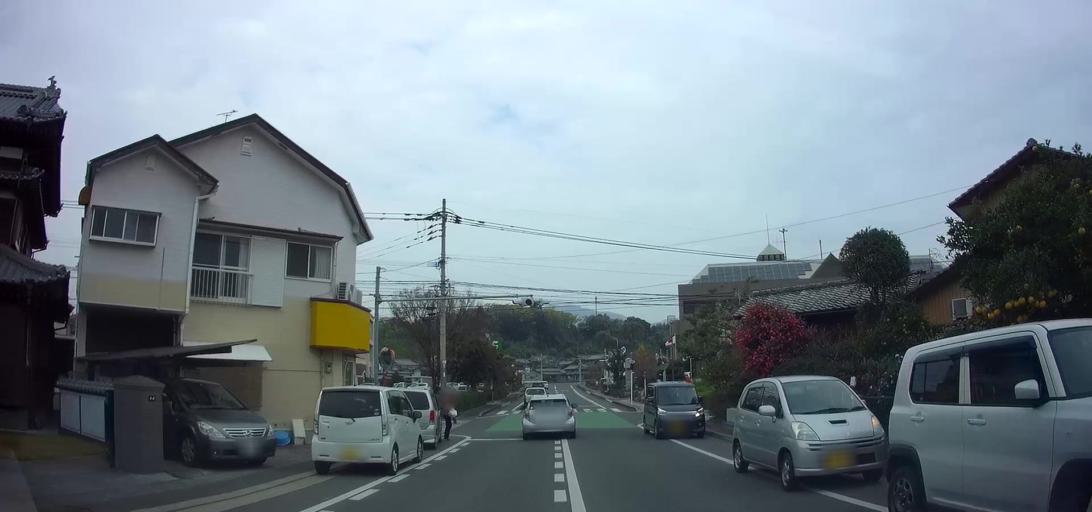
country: JP
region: Nagasaki
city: Shimabara
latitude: 32.6587
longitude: 130.2979
